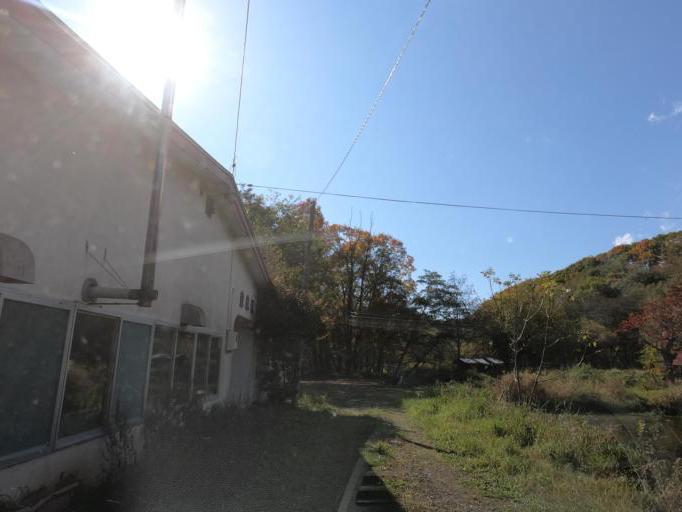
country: JP
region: Hokkaido
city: Otofuke
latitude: 43.2335
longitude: 143.2628
